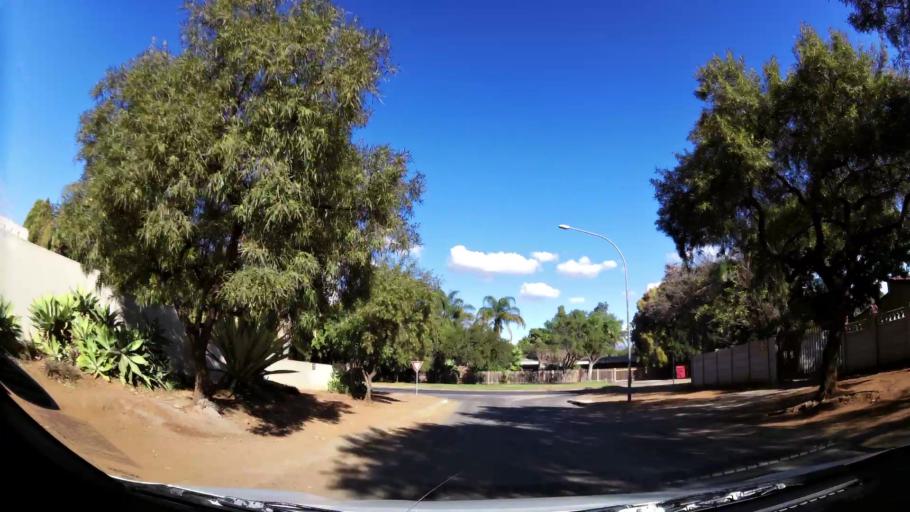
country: ZA
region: Limpopo
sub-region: Capricorn District Municipality
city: Polokwane
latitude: -23.9121
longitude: 29.4826
